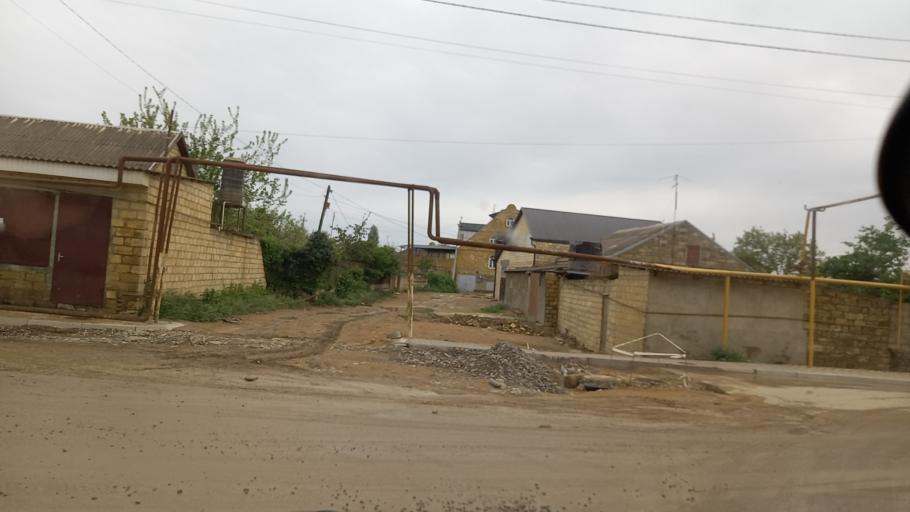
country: RU
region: Dagestan
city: Derbent
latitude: 42.1008
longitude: 48.2820
